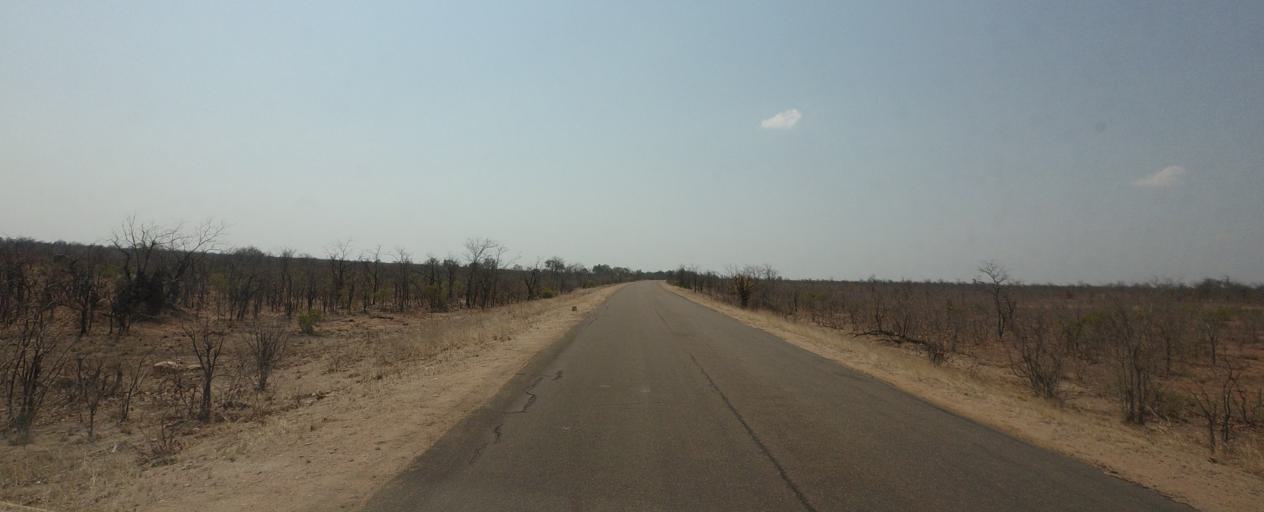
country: ZA
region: Limpopo
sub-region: Mopani District Municipality
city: Phalaborwa
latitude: -23.3753
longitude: 31.3221
